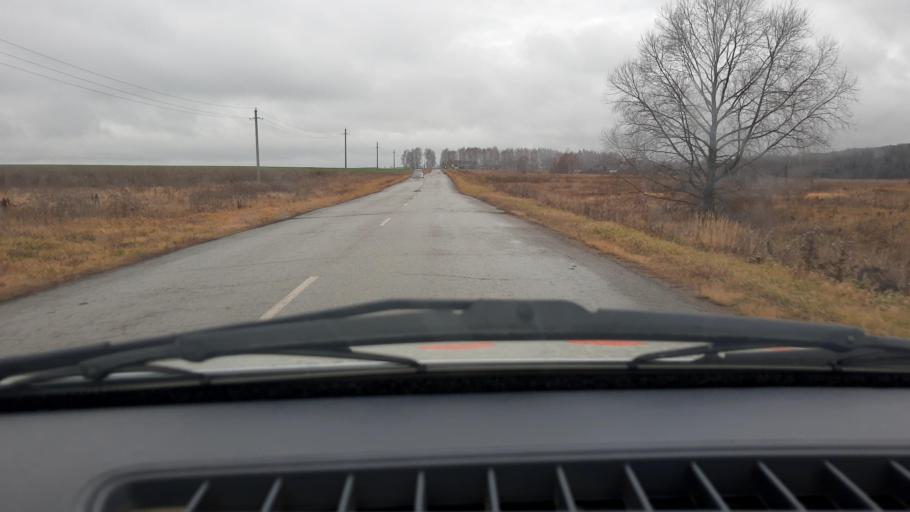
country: RU
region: Bashkortostan
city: Iglino
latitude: 54.7643
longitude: 56.3846
